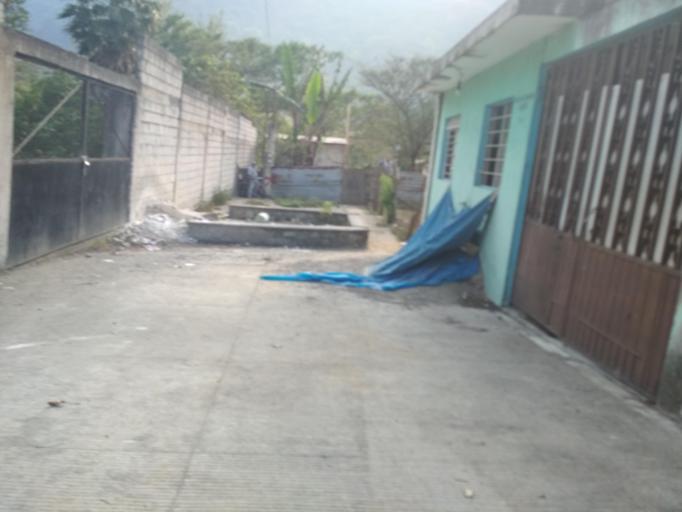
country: MX
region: Veracruz
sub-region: Ixhuatlancillo
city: Fraccionamiento Valle Dorado
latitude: 18.8663
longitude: -97.1187
